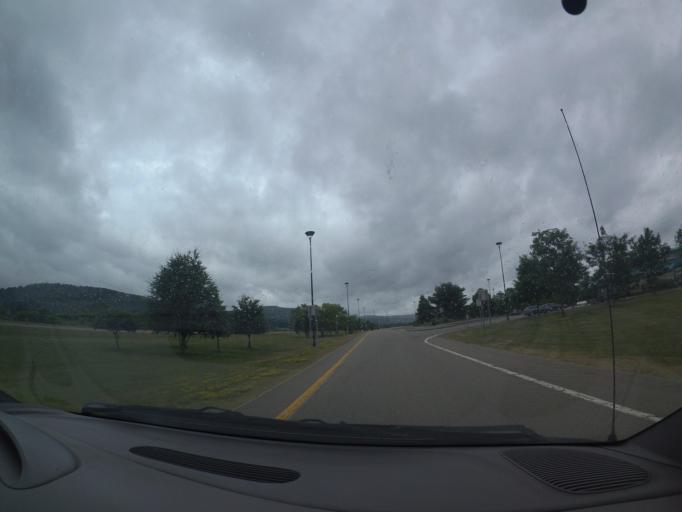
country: US
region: New York
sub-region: Cattaraugus County
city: Allegany
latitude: 42.0960
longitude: -78.5350
